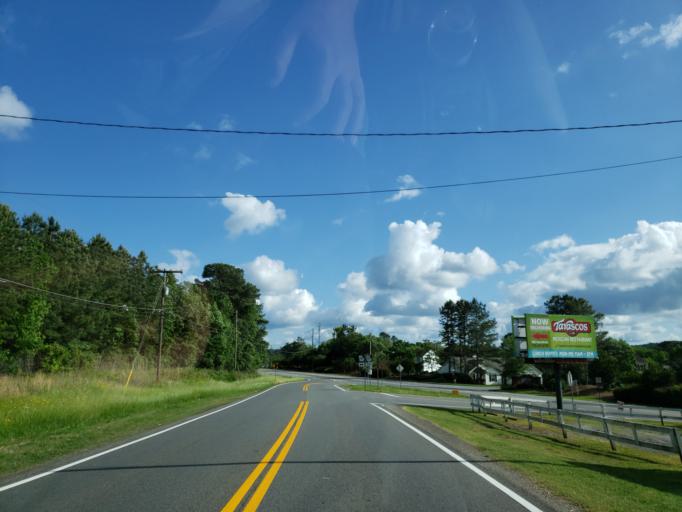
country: US
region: Georgia
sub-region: Bartow County
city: Cartersville
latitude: 34.2278
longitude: -84.8567
